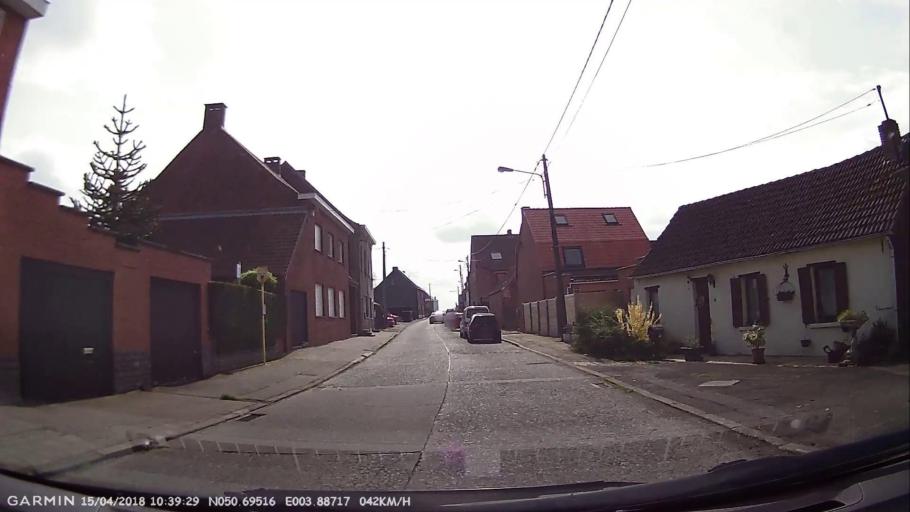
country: BE
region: Wallonia
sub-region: Province du Hainaut
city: Lessines
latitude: 50.6951
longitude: 3.8872
